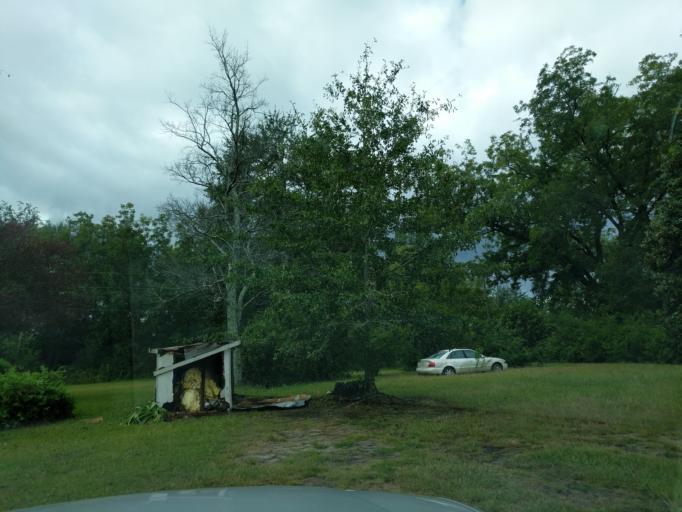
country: US
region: Georgia
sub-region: Wilkes County
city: Washington
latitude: 33.6760
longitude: -82.6241
